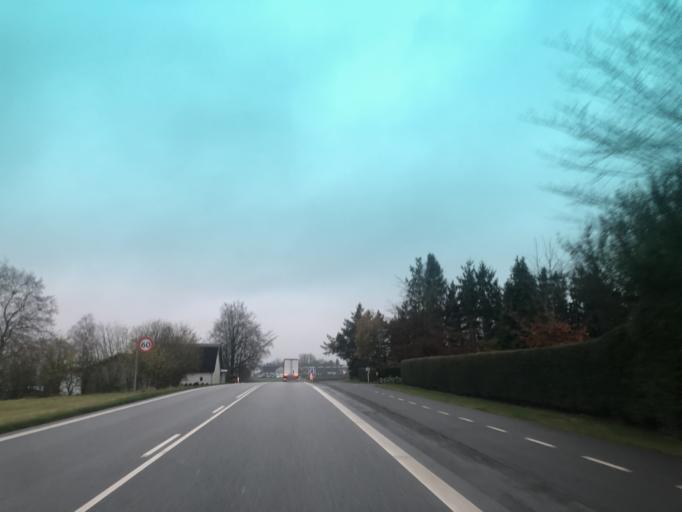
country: DK
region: South Denmark
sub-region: Nyborg Kommune
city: Ullerslev
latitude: 55.2681
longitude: 10.6758
